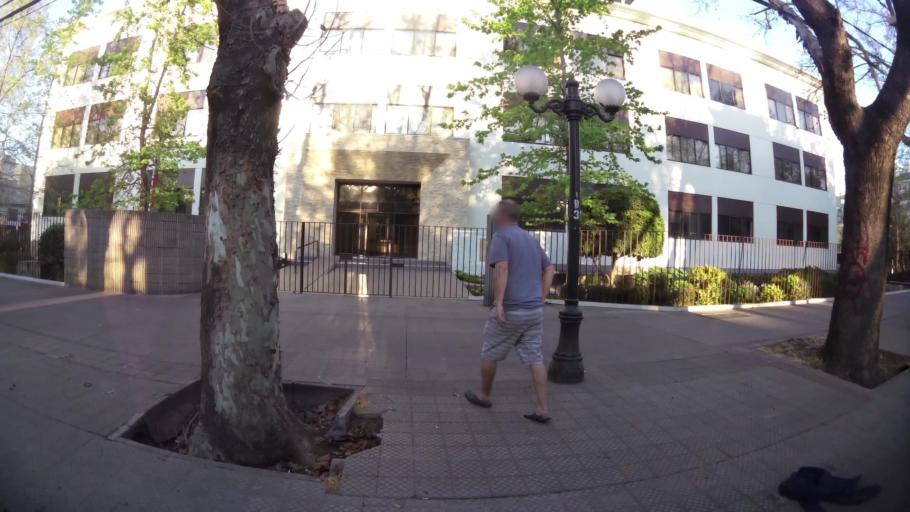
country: CL
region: Santiago Metropolitan
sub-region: Provincia de Santiago
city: Villa Presidente Frei, Nunoa, Santiago, Chile
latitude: -33.4358
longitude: -70.6083
